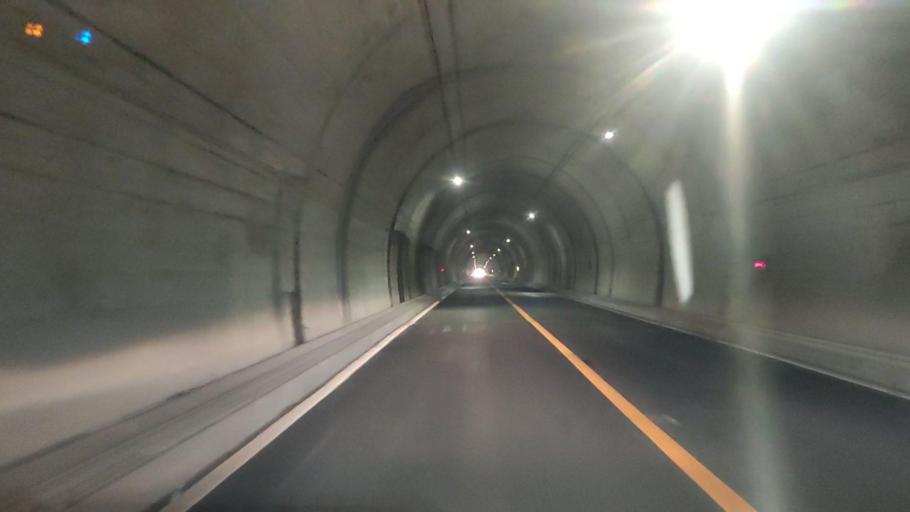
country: JP
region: Oita
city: Saiki
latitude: 32.8808
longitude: 131.9479
